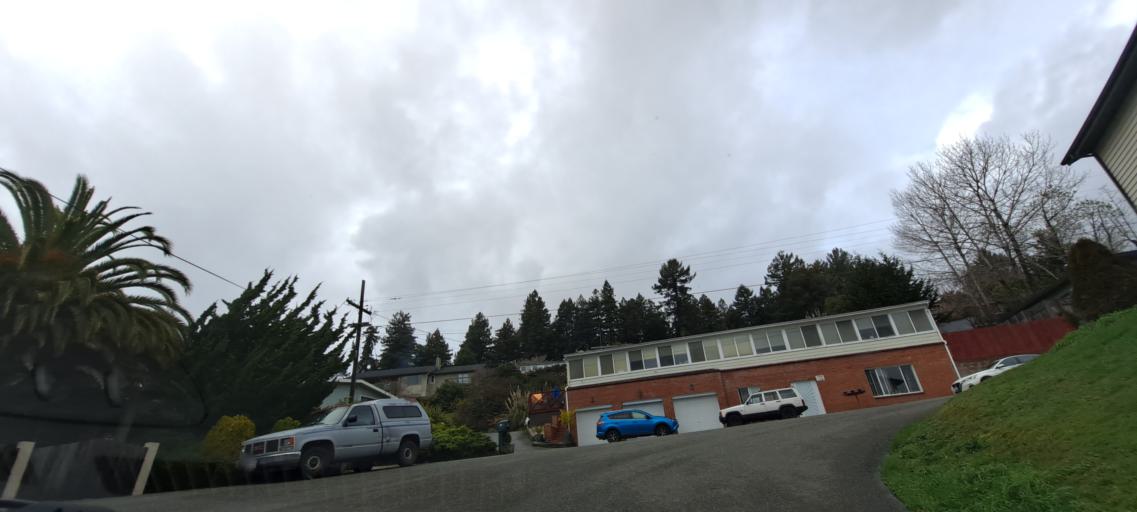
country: US
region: California
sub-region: Humboldt County
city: Fortuna
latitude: 40.5982
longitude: -124.1462
